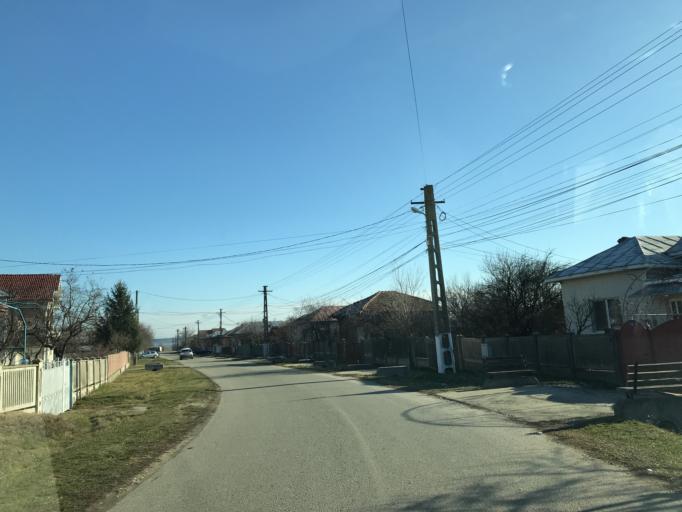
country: RO
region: Olt
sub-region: Comuna Slatioara
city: Slatioara
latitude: 44.3969
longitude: 24.3220
